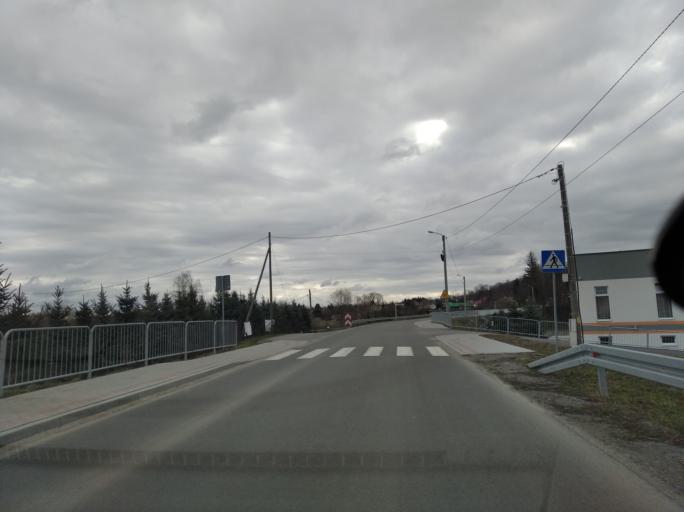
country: PL
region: Subcarpathian Voivodeship
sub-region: Powiat rzeszowski
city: Siedliska
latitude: 49.9509
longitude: 21.9310
